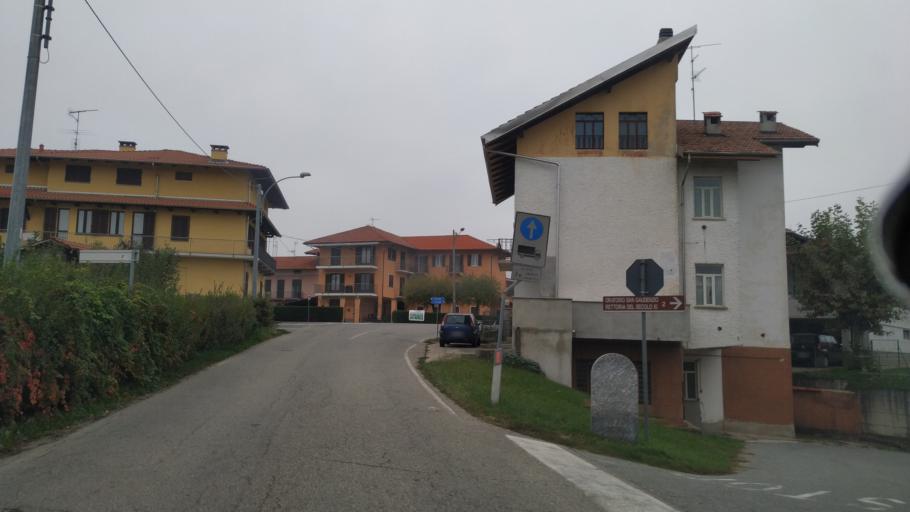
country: IT
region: Piedmont
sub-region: Provincia di Biella
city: Lessona
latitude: 45.5764
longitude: 8.2031
